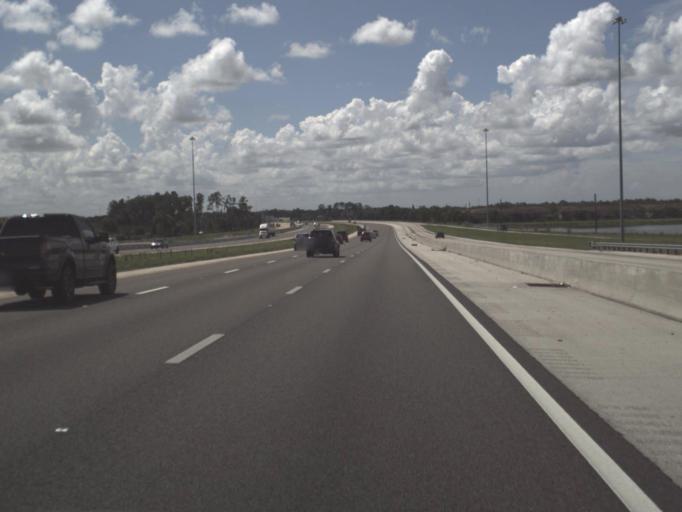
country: US
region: Florida
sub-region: Lee County
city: Three Oaks
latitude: 26.4904
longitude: -81.7946
